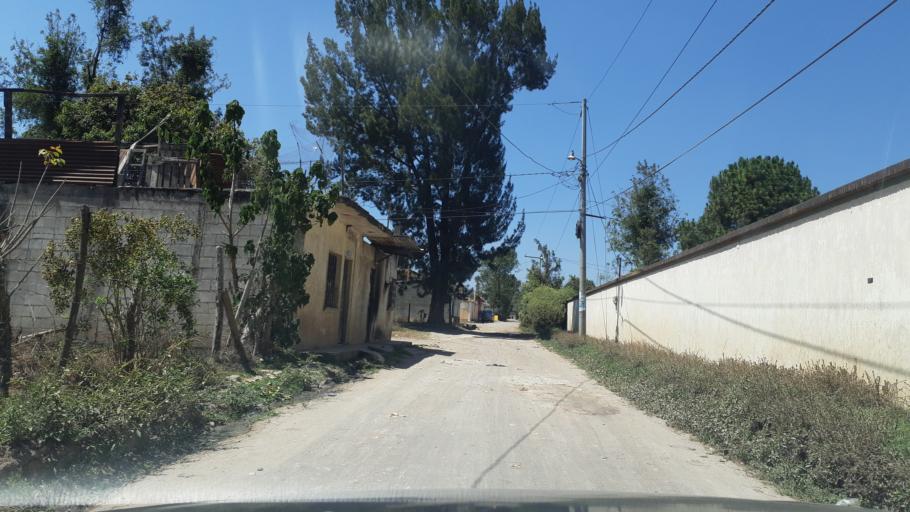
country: GT
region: Chimaltenango
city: El Tejar
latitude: 14.6510
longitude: -90.8077
